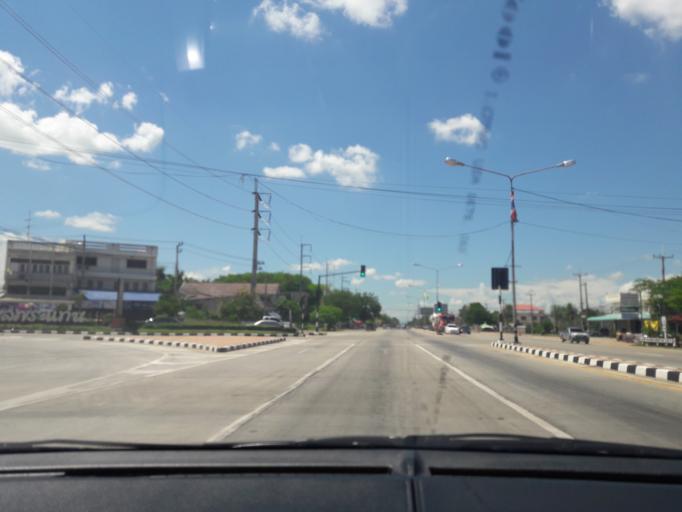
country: TH
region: Kanchanaburi
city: Tha Maka
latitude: 14.0385
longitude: 99.7910
